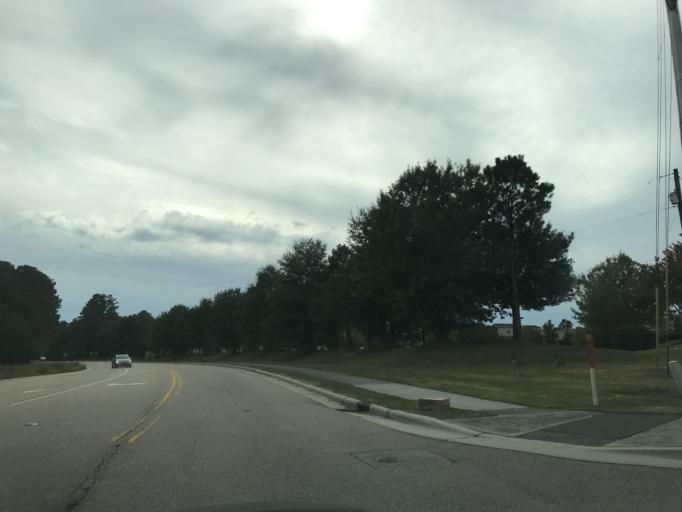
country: US
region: North Carolina
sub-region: Wake County
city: Rolesville
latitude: 35.8931
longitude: -78.5079
